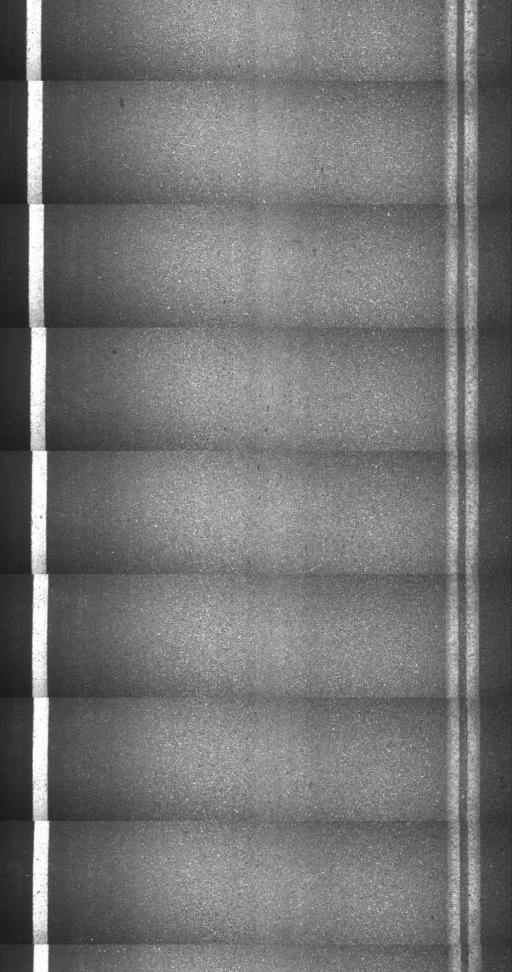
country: US
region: Vermont
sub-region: Caledonia County
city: Lyndonville
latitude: 44.7408
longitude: -71.8831
